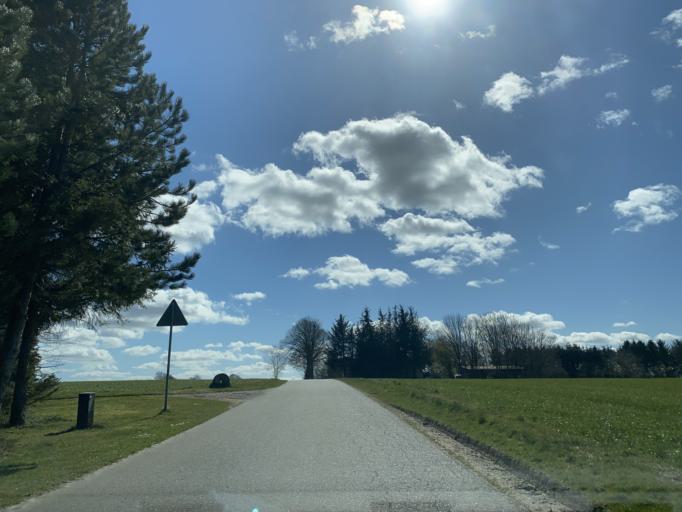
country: DK
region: Central Jutland
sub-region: Favrskov Kommune
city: Ulstrup
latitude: 56.3321
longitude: 9.7876
